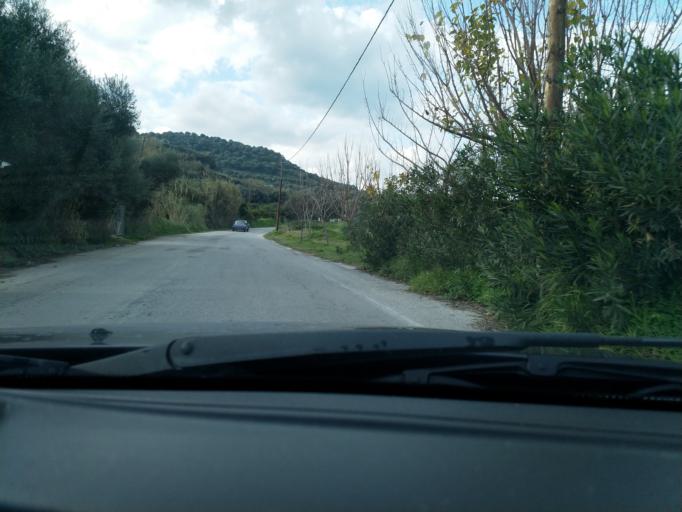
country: GR
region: Crete
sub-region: Nomos Chanias
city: Gerani
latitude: 35.4989
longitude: 23.9012
